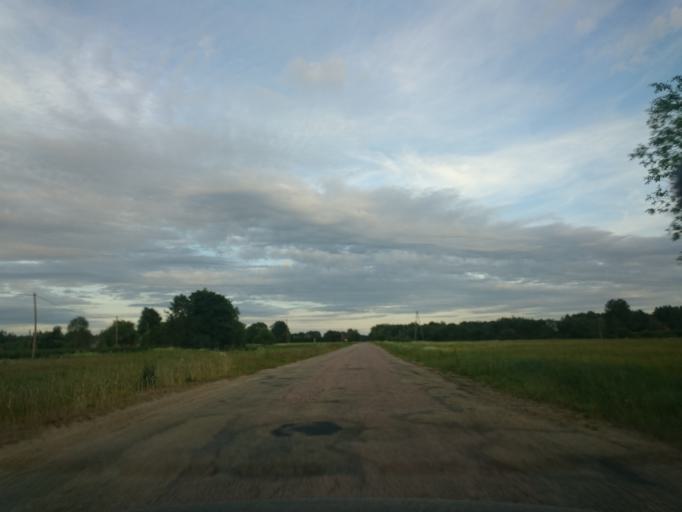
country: LV
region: Ropazu
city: Ropazi
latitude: 56.9675
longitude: 24.6774
